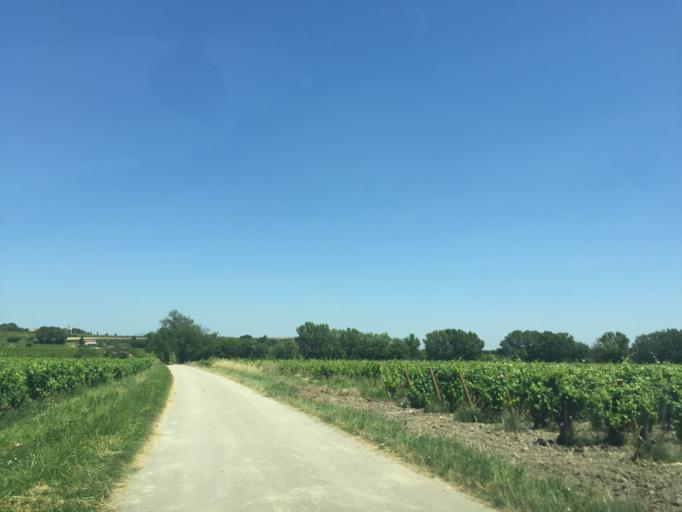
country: FR
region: Languedoc-Roussillon
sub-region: Departement du Gard
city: Roquemaure
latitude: 44.0574
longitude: 4.7968
